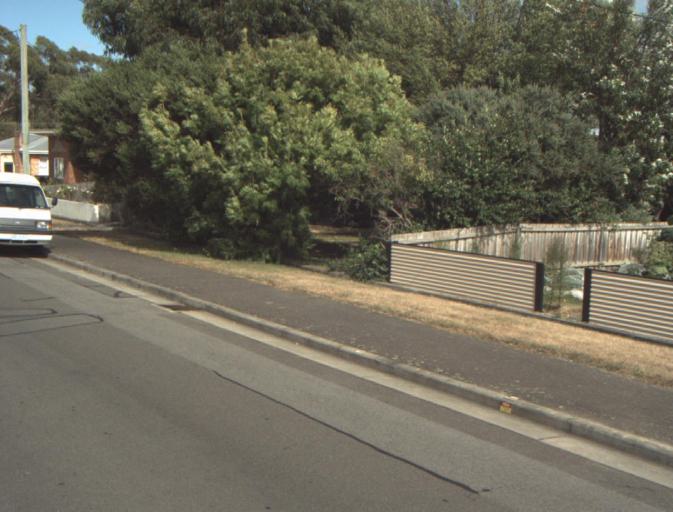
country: AU
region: Tasmania
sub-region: Launceston
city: Summerhill
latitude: -41.4708
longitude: 147.1208
